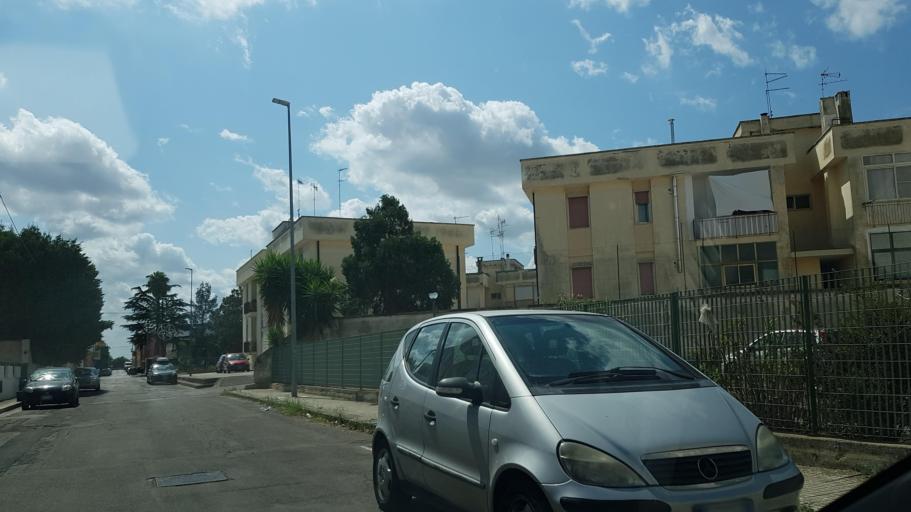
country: IT
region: Apulia
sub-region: Provincia di Lecce
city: Trepuzzi
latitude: 40.4088
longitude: 18.0627
